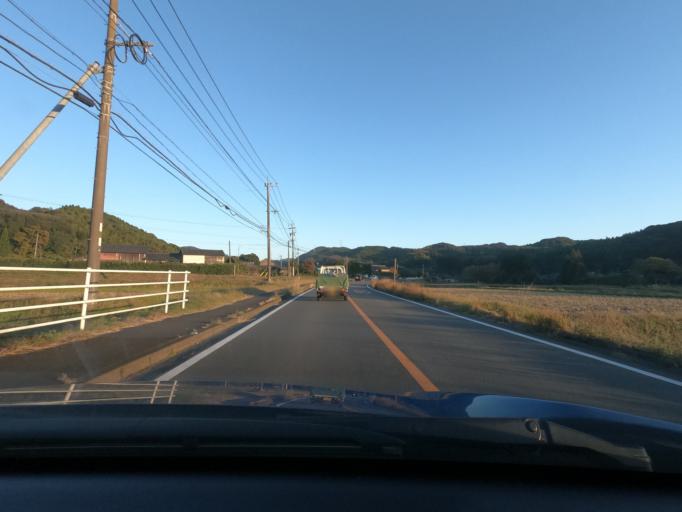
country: JP
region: Kagoshima
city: Satsumasendai
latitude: 31.7935
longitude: 130.4501
